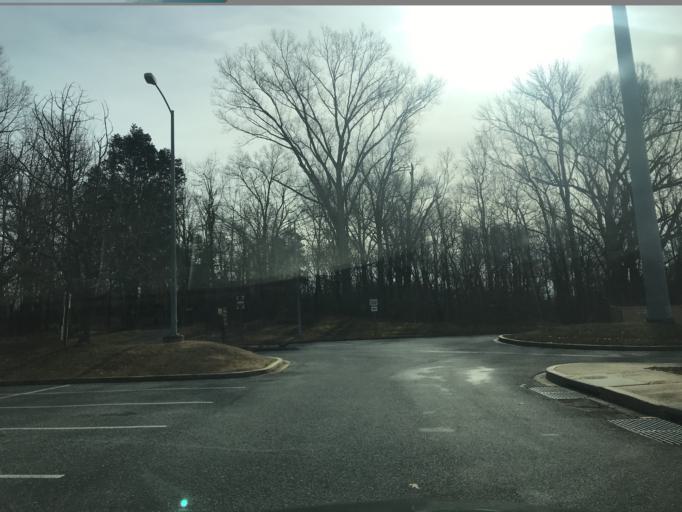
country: US
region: Virginia
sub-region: King George County
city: Dahlgren
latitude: 38.3692
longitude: -76.9606
